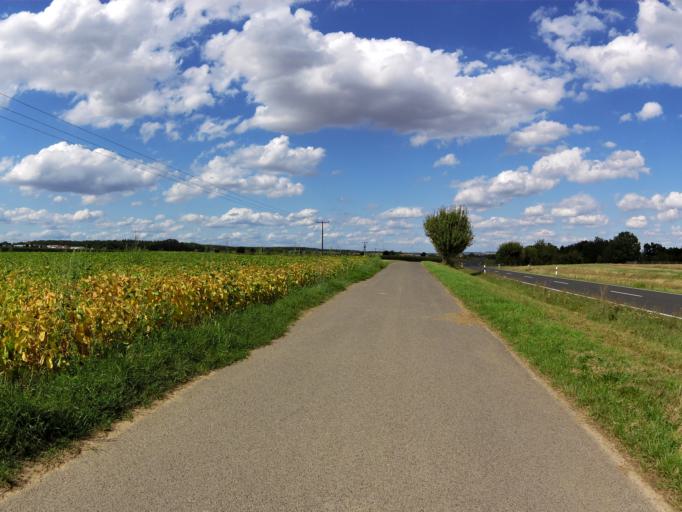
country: DE
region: Bavaria
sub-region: Regierungsbezirk Unterfranken
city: Bergrheinfeld
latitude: 49.9880
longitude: 10.1694
